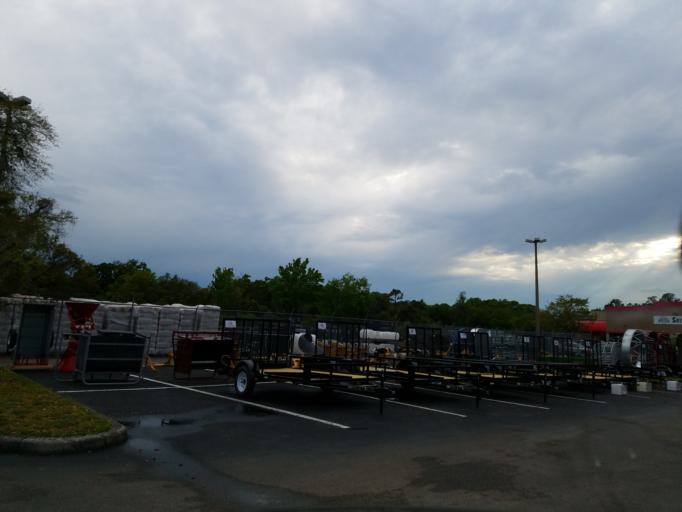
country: US
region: Florida
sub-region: Hillsborough County
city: Plant City
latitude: 27.9961
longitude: -82.1225
